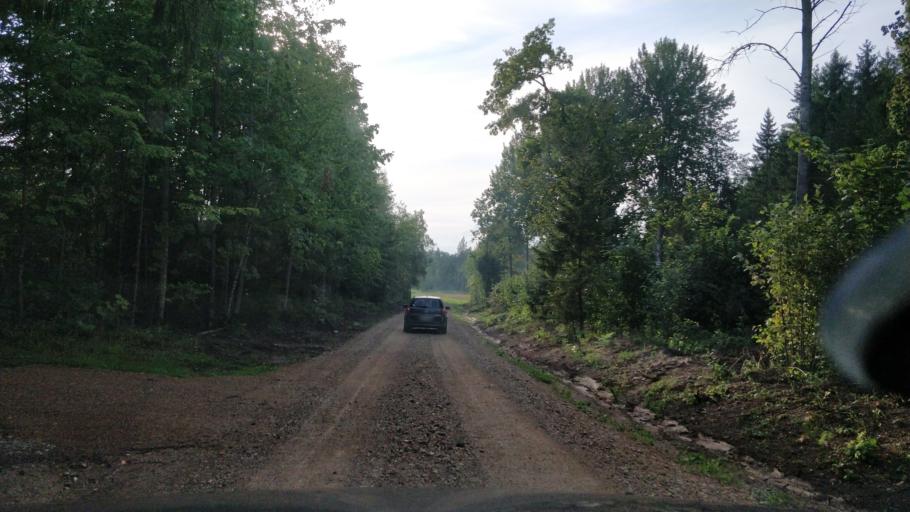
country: LV
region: Sigulda
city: Sigulda
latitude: 57.1003
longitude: 24.7916
